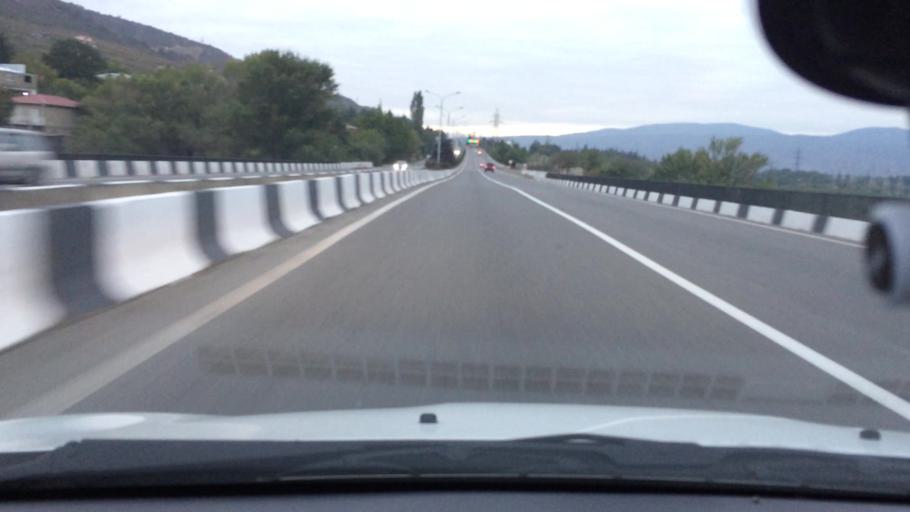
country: GE
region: Mtskheta-Mtianeti
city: Mtskheta
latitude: 41.8734
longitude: 44.7267
